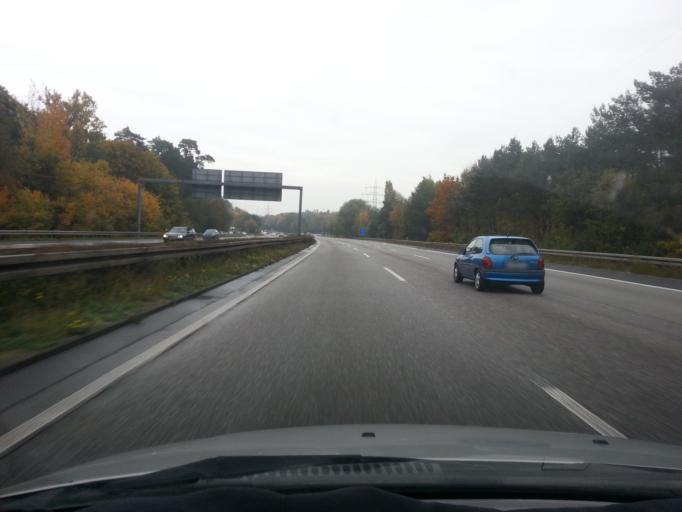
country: DE
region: Hesse
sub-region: Regierungsbezirk Darmstadt
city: Offenbach
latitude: 50.0749
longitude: 8.7345
